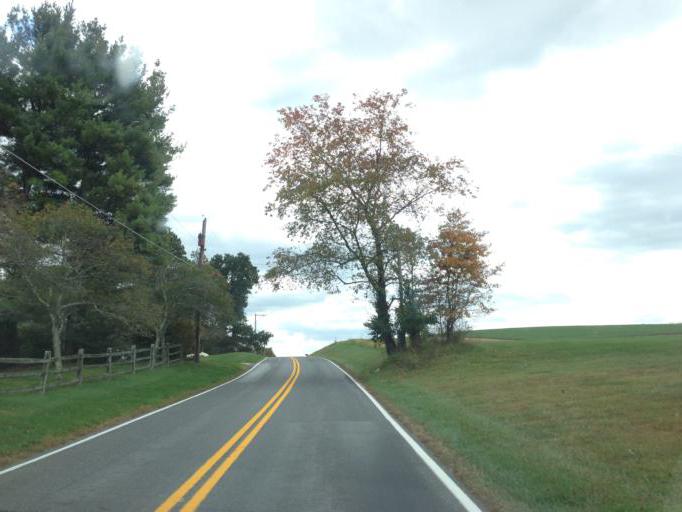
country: US
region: Maryland
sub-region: Carroll County
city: Mount Airy
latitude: 39.2828
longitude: -77.0883
